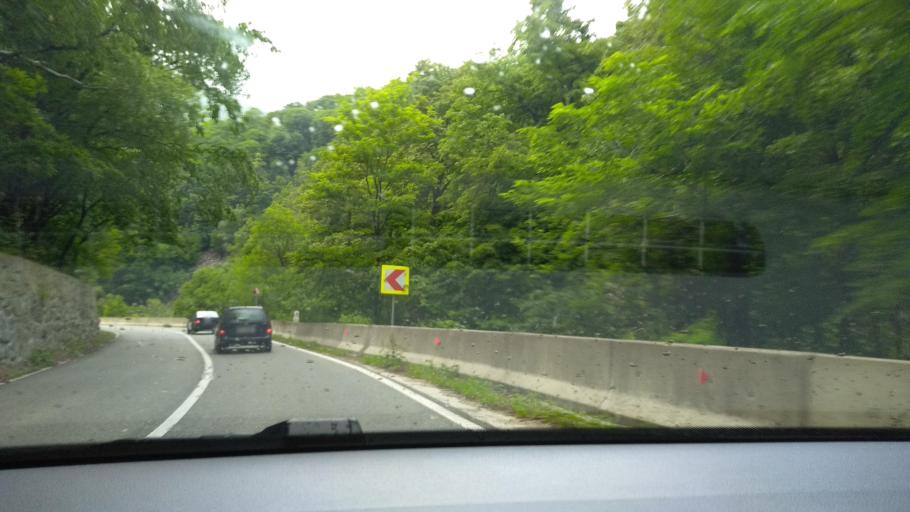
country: RO
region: Hunedoara
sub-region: Comuna Aninoasa
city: Iscroni
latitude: 45.3187
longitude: 23.3750
